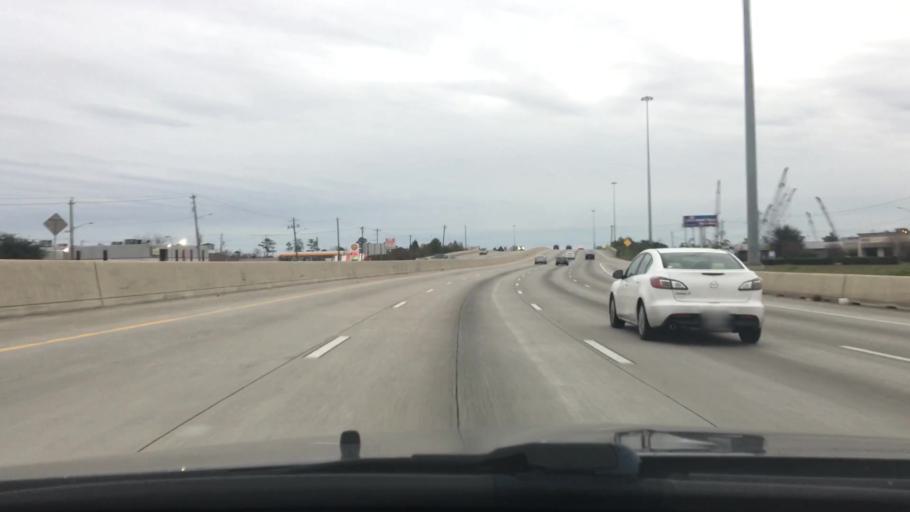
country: US
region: Texas
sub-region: Harris County
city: Houston
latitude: 29.8089
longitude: -95.3050
